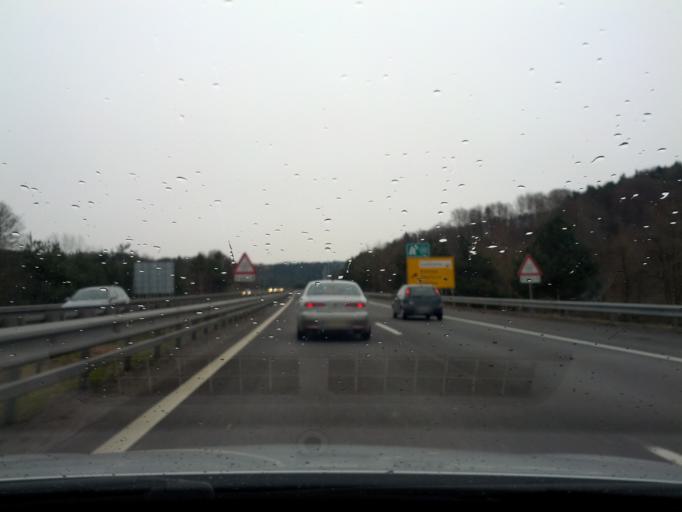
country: SI
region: Skofljica
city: Lavrica
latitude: 46.0145
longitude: 14.5389
